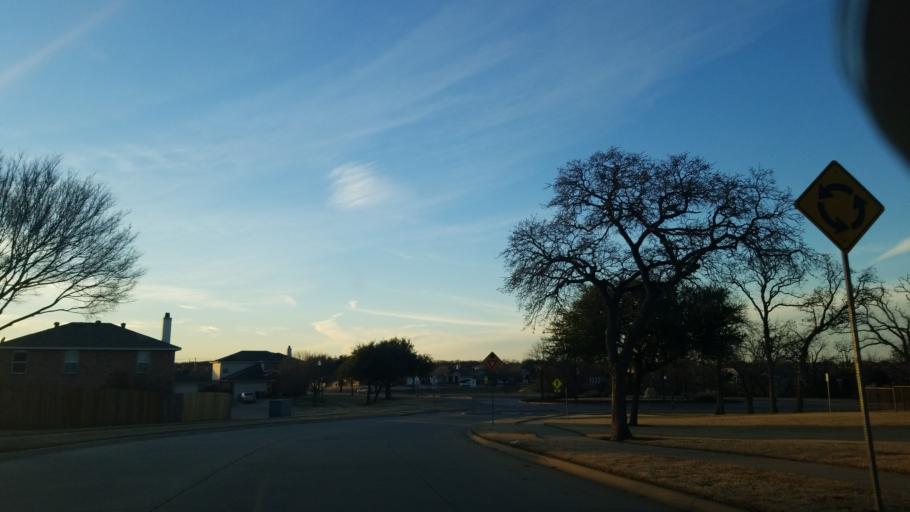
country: US
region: Texas
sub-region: Denton County
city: Corinth
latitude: 33.1540
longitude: -97.1018
